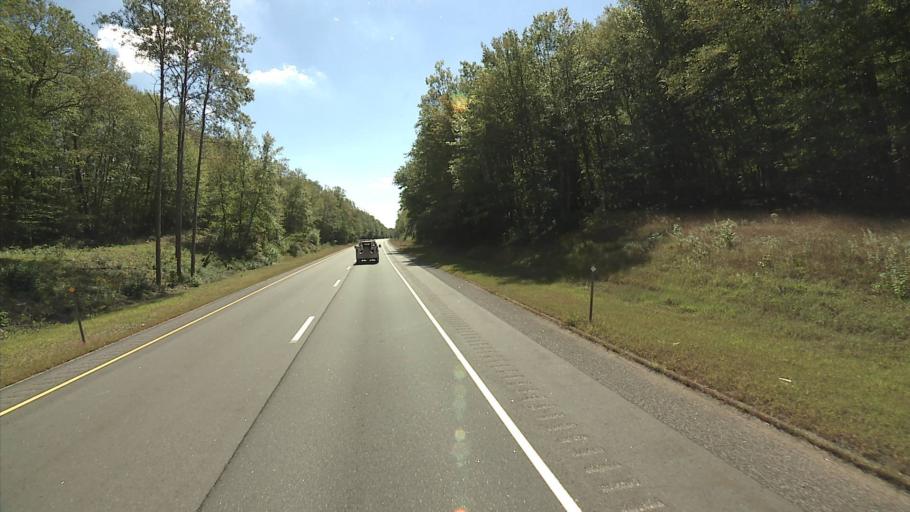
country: US
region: Connecticut
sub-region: New London County
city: Colchester
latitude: 41.5155
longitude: -72.3034
